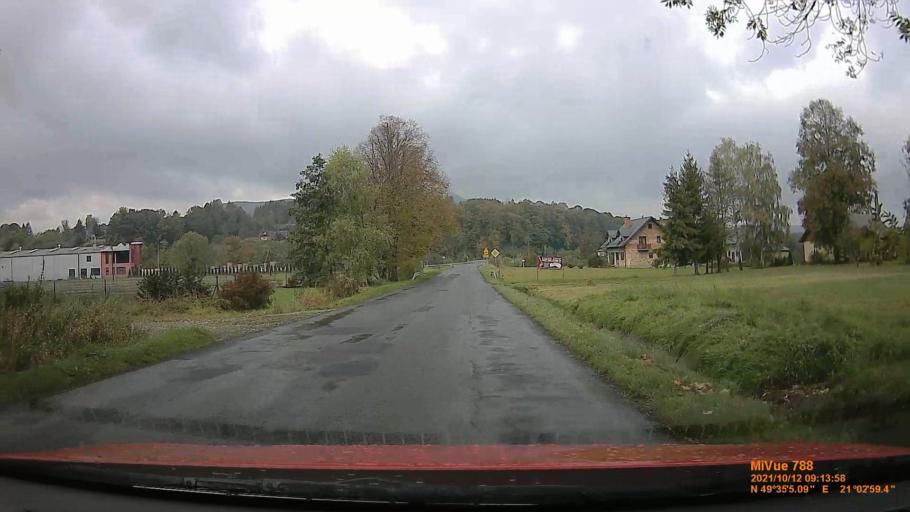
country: PL
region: Lesser Poland Voivodeship
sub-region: Powiat gorlicki
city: Ropa
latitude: 49.5848
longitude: 21.0496
